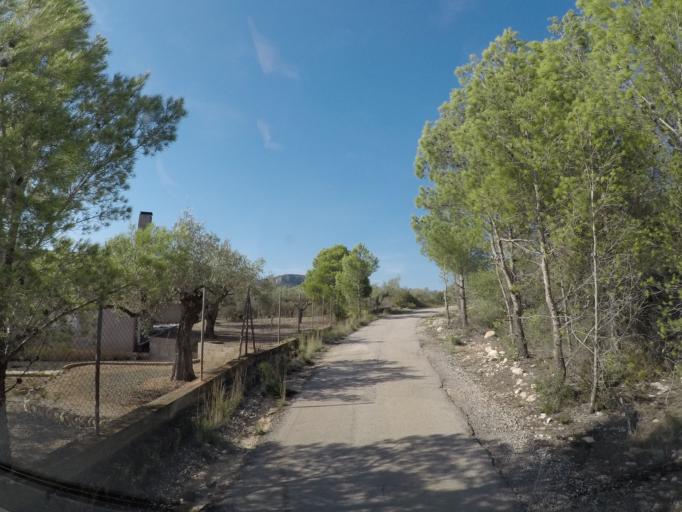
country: ES
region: Catalonia
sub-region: Provincia de Tarragona
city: El Perello
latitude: 40.9108
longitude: 0.7238
